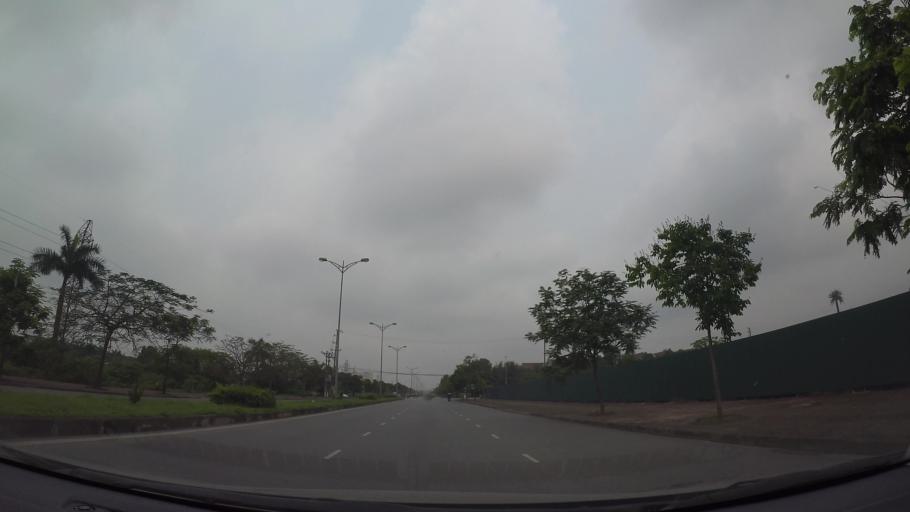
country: VN
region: Ha Noi
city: Trau Quy
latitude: 21.0364
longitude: 105.9218
